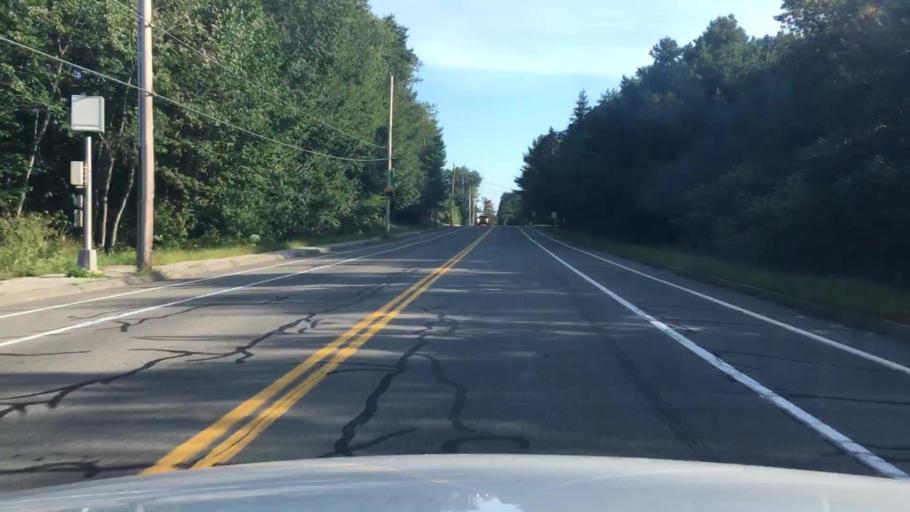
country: US
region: Maine
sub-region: Cumberland County
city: Falmouth
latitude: 43.7209
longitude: -70.2935
